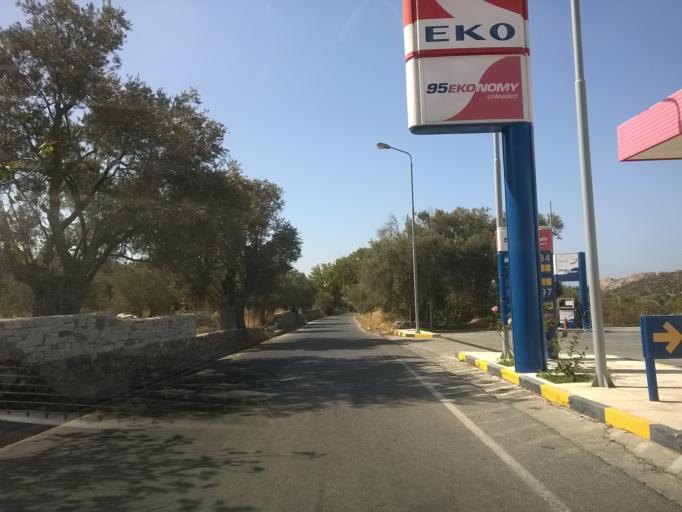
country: GR
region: South Aegean
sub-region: Nomos Kykladon
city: Filotion
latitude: 37.0673
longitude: 25.4893
